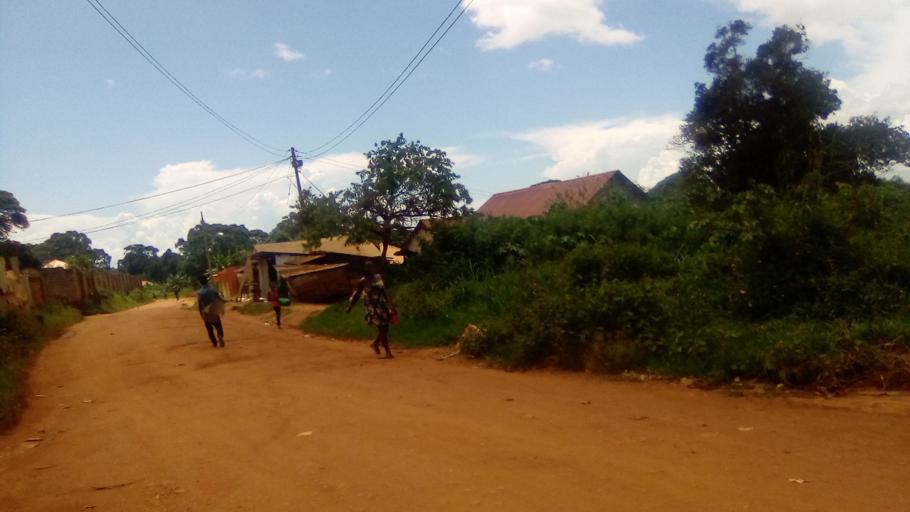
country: UG
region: Central Region
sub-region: Wakiso District
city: Entebbe
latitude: 0.1024
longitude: 32.5247
